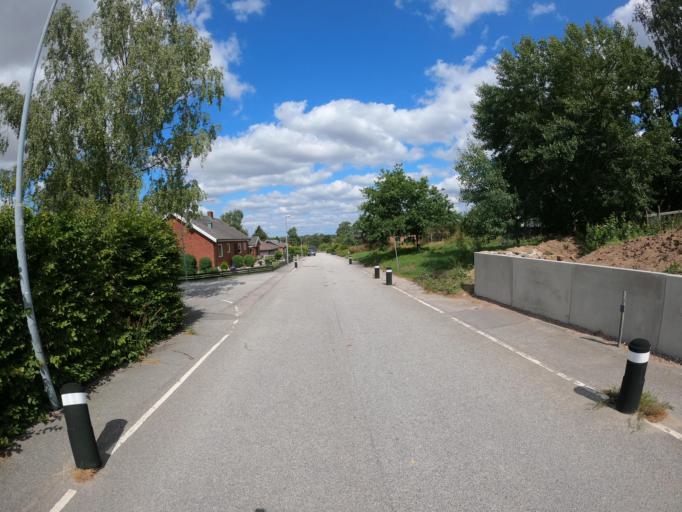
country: SE
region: Skane
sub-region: Lunds Kommun
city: Genarp
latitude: 55.5951
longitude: 13.4005
